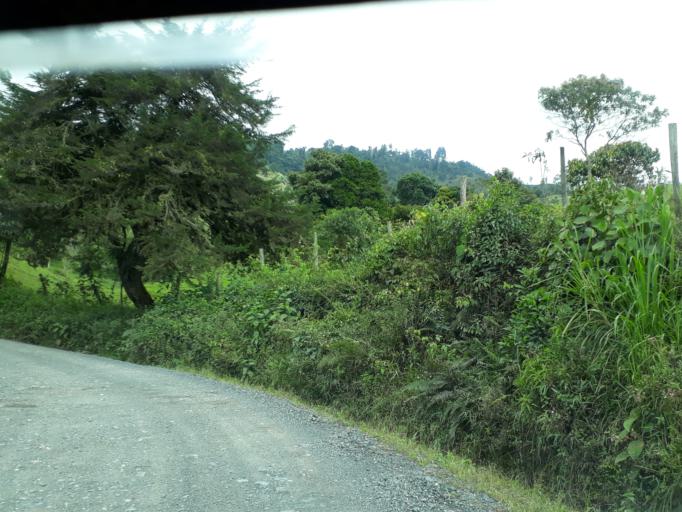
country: CO
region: Cundinamarca
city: Pacho
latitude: 5.2575
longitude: -74.1858
